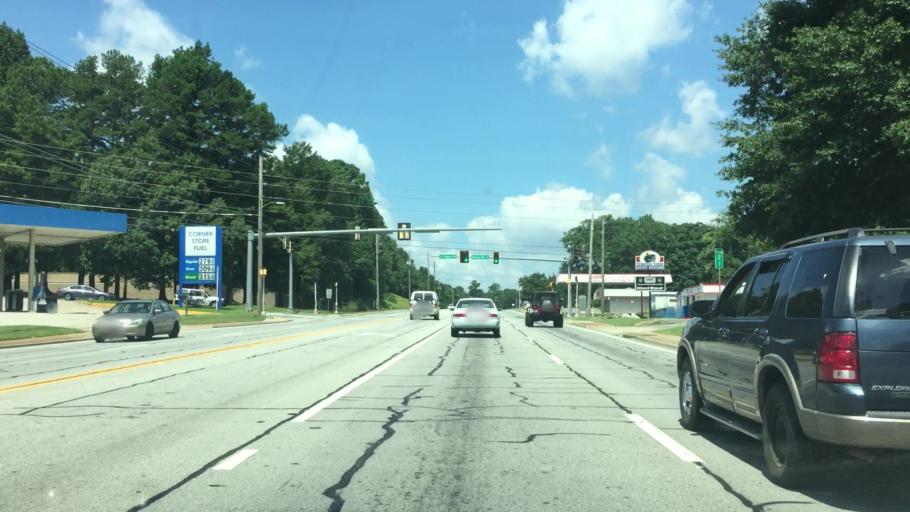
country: US
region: Georgia
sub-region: Henry County
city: Stockbridge
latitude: 33.5449
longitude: -84.2439
